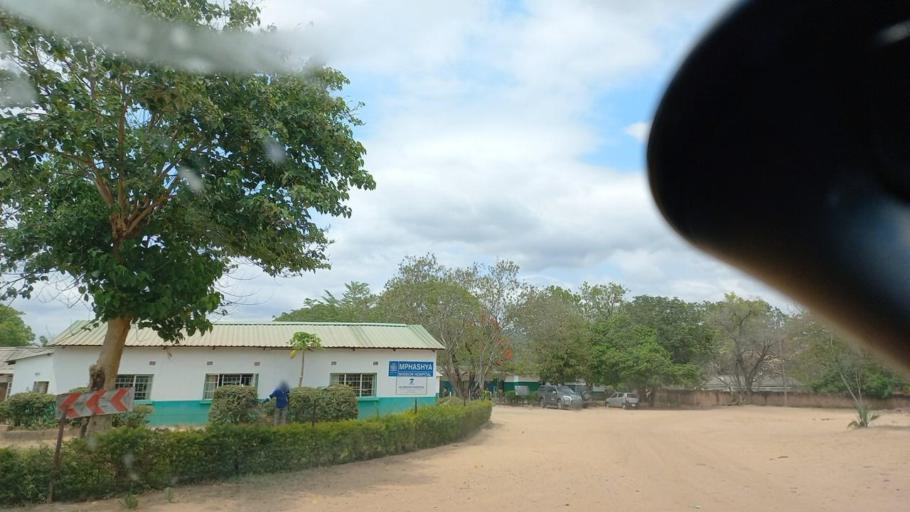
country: ZM
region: Lusaka
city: Luangwa
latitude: -15.1079
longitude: 29.7251
